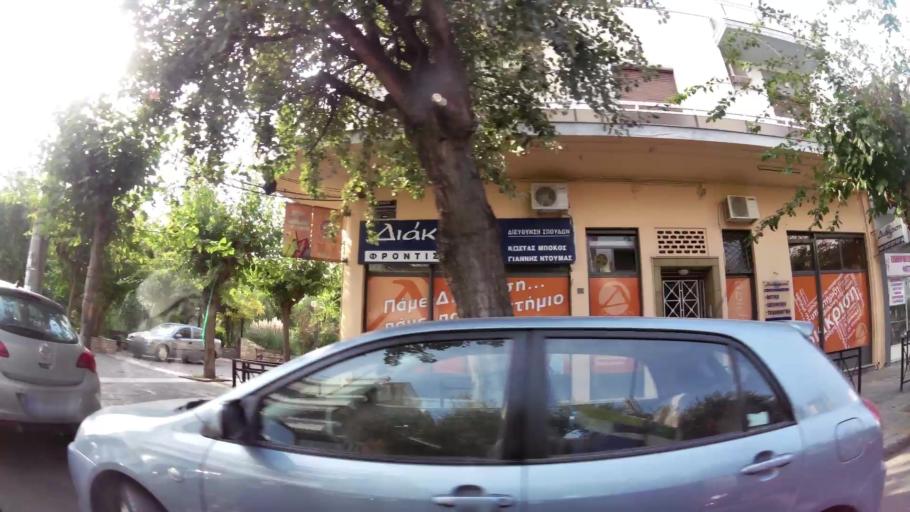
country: GR
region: Attica
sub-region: Nomarchia Athinas
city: Kallithea
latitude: 37.9527
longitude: 23.6914
